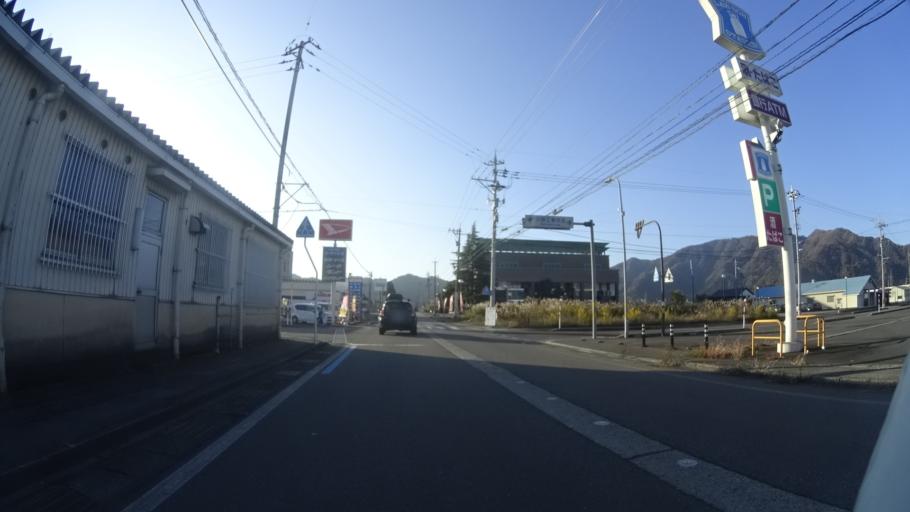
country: JP
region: Fukui
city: Ono
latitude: 35.9913
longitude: 136.4828
